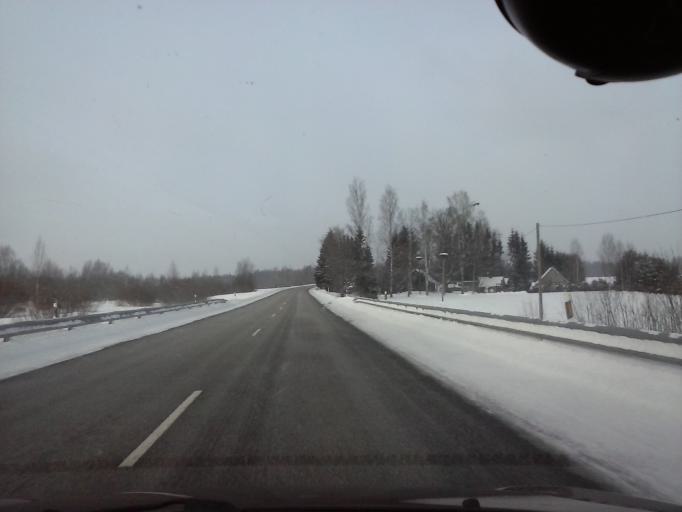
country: EE
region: Paernumaa
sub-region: Saarde vald
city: Kilingi-Nomme
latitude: 58.1998
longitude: 25.0631
